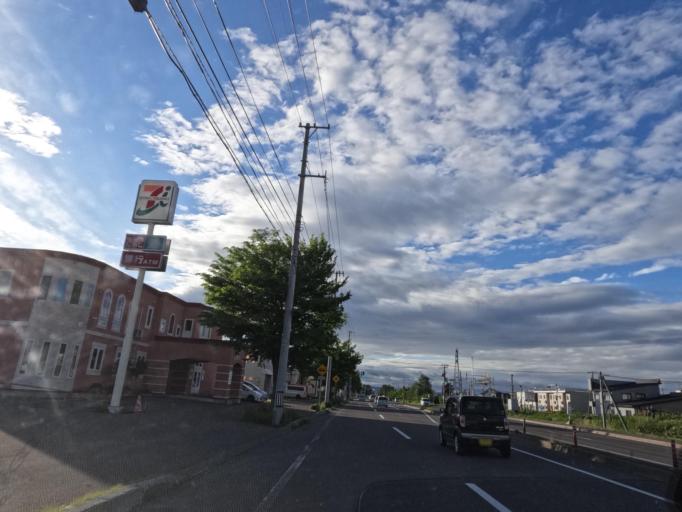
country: JP
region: Hokkaido
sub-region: Asahikawa-shi
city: Asahikawa
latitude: 43.7388
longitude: 142.3607
